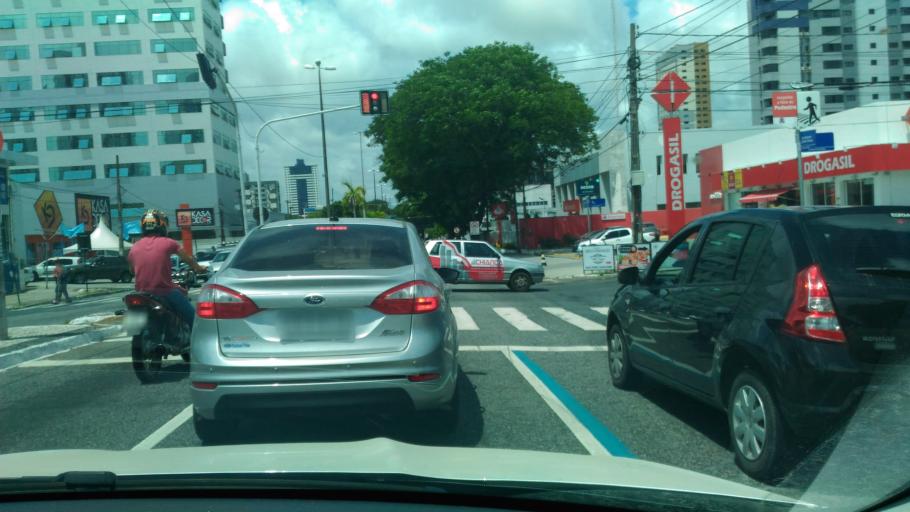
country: BR
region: Paraiba
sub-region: Joao Pessoa
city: Joao Pessoa
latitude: -7.1197
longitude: -34.8531
